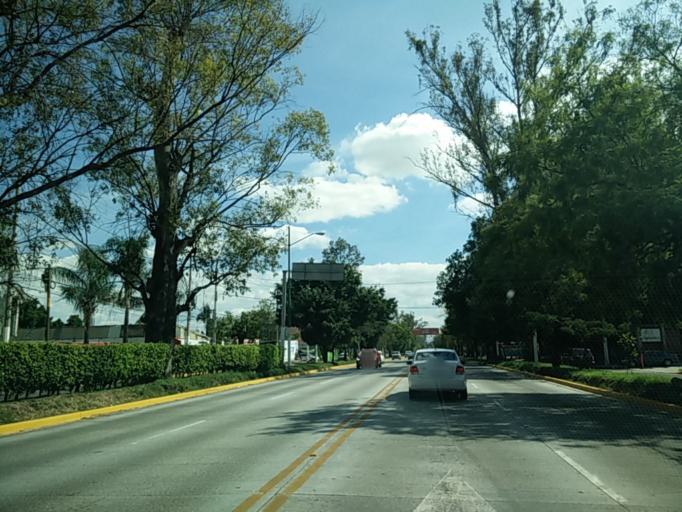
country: MX
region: Jalisco
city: Zapopan2
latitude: 20.6902
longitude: -103.4488
